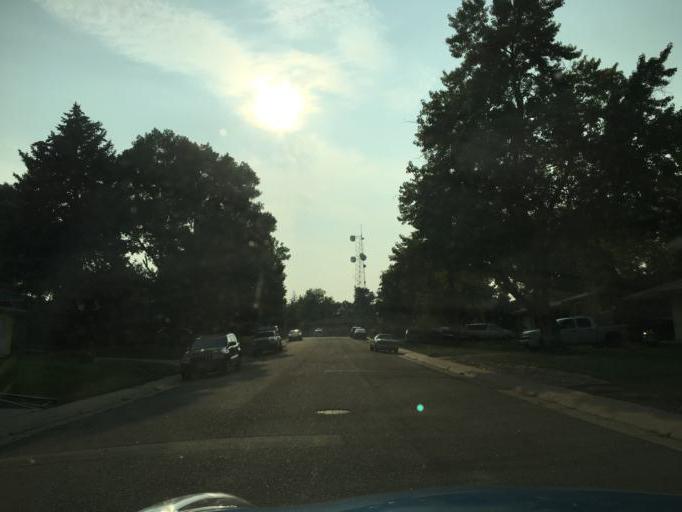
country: US
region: Colorado
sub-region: Arapahoe County
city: Glendale
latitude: 39.6918
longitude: -104.9330
